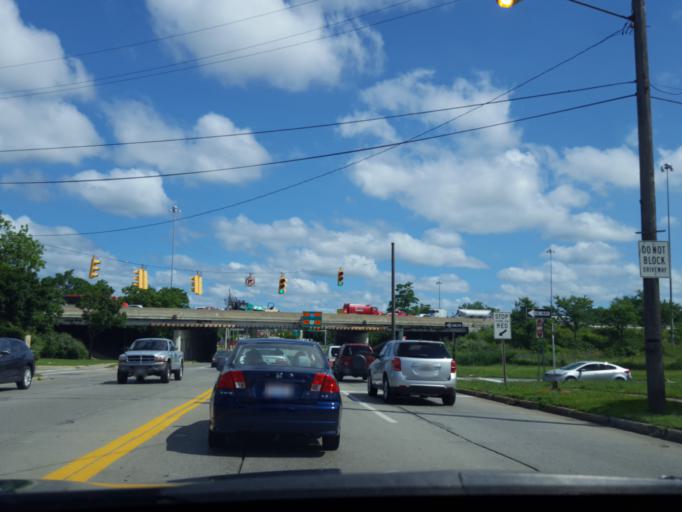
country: US
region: Ohio
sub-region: Cuyahoga County
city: Euclid
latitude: 41.5772
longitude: -81.5501
